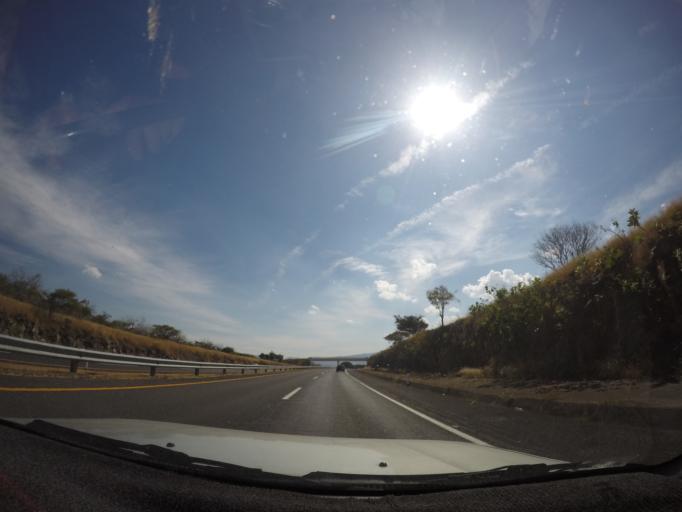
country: MX
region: Michoacan
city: Penjamillo de Degollado
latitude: 20.0313
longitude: -101.9230
